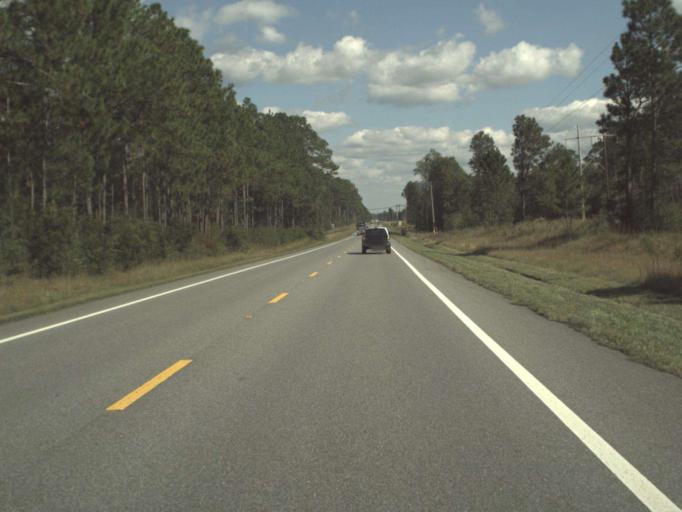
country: US
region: Florida
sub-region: Walton County
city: Freeport
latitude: 30.4759
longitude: -86.0204
